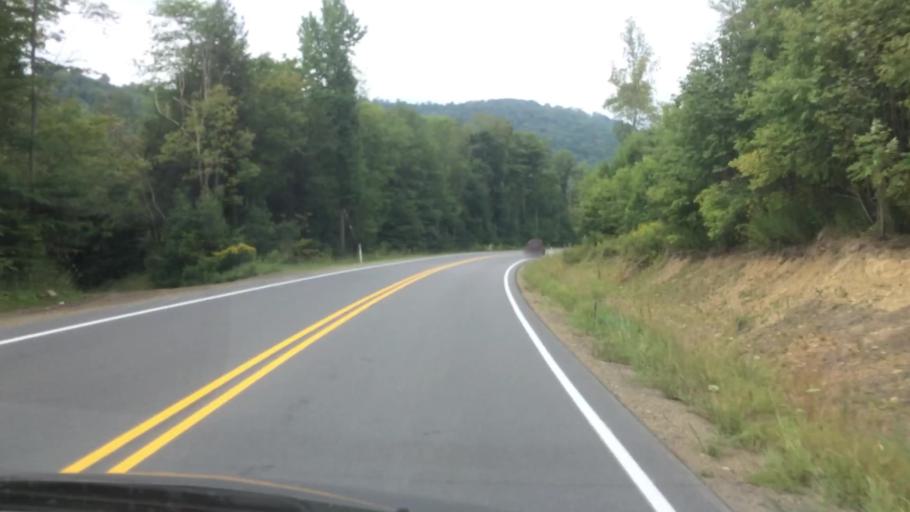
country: US
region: Pennsylvania
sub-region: McKean County
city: Bradford
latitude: 41.8877
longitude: -78.5979
